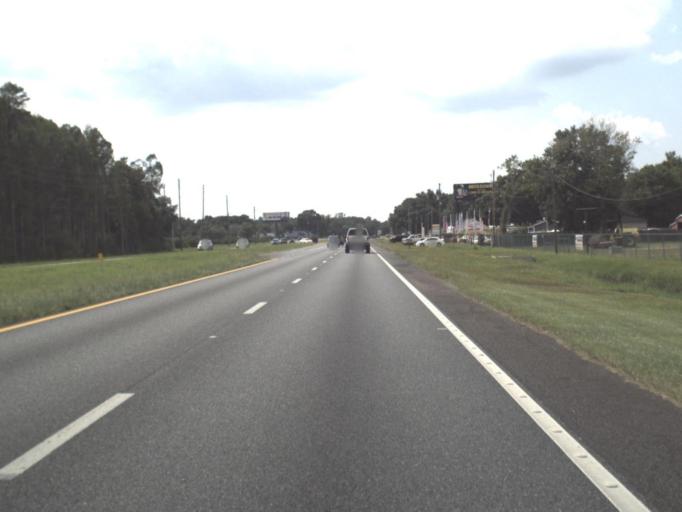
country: US
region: Florida
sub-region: Pasco County
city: Land O' Lakes
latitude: 28.2524
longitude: -82.4679
